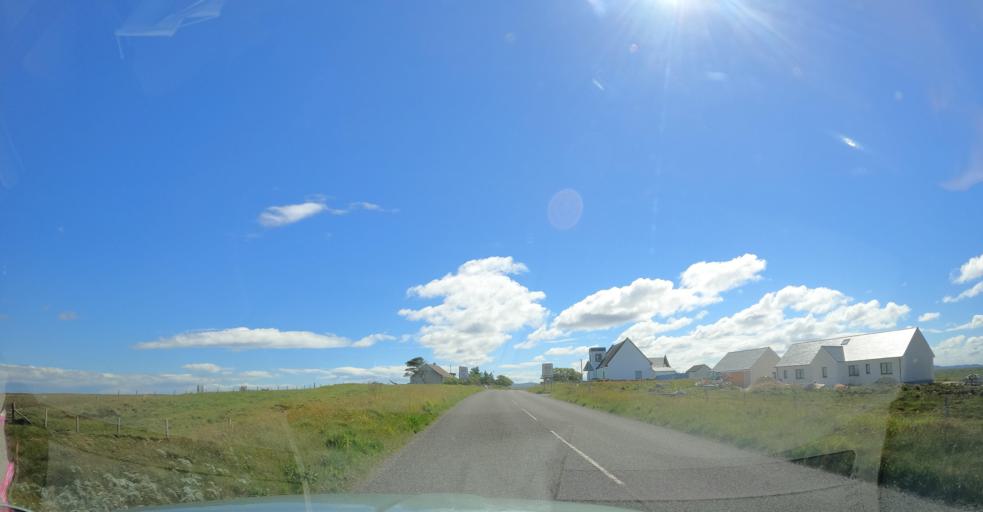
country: GB
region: Scotland
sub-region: Eilean Siar
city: Isle of Lewis
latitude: 58.3708
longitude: -6.5056
